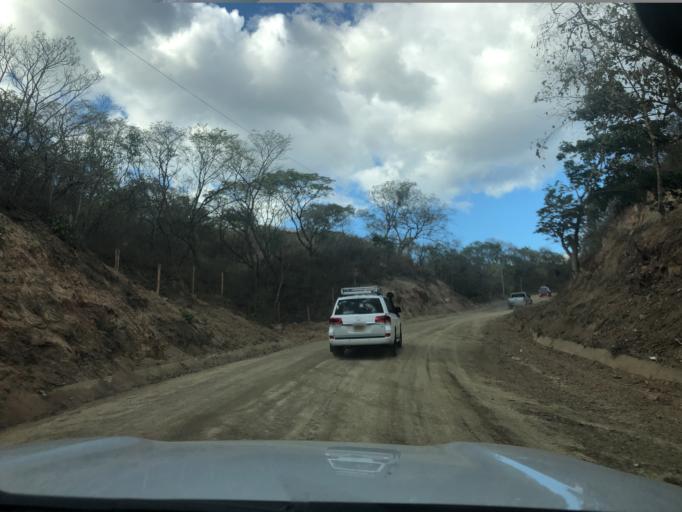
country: NI
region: Nueva Segovia
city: Ocotal
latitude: 13.6571
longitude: -86.6151
